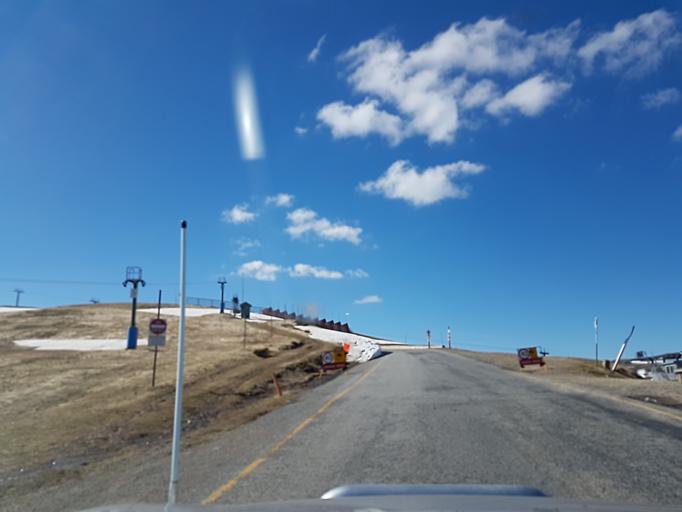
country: AU
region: Victoria
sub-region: Alpine
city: Mount Beauty
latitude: -36.9809
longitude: 147.1421
